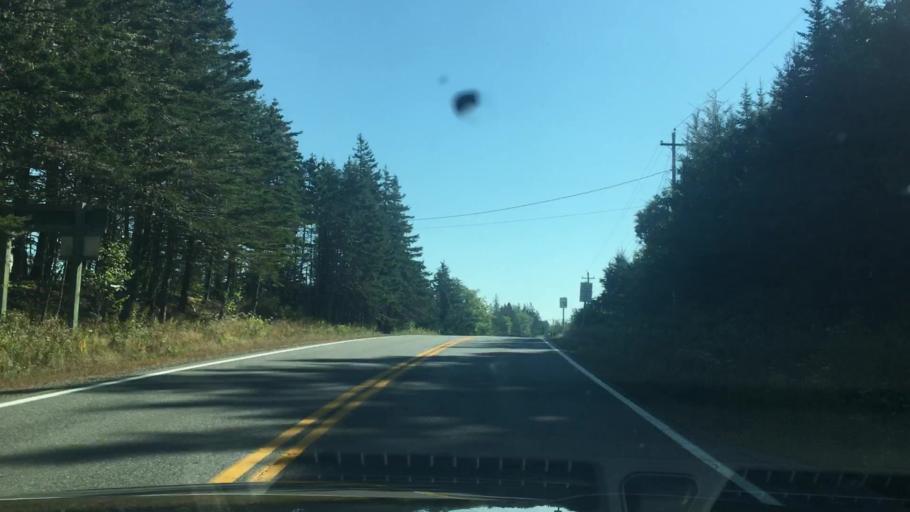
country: CA
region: Nova Scotia
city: Cole Harbour
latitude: 44.7793
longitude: -63.0062
